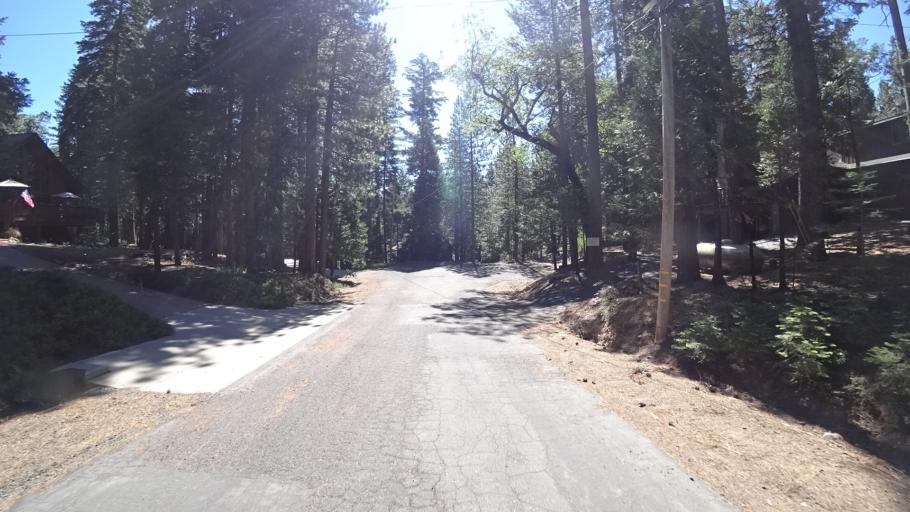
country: US
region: California
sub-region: Calaveras County
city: Arnold
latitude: 38.2810
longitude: -120.2825
